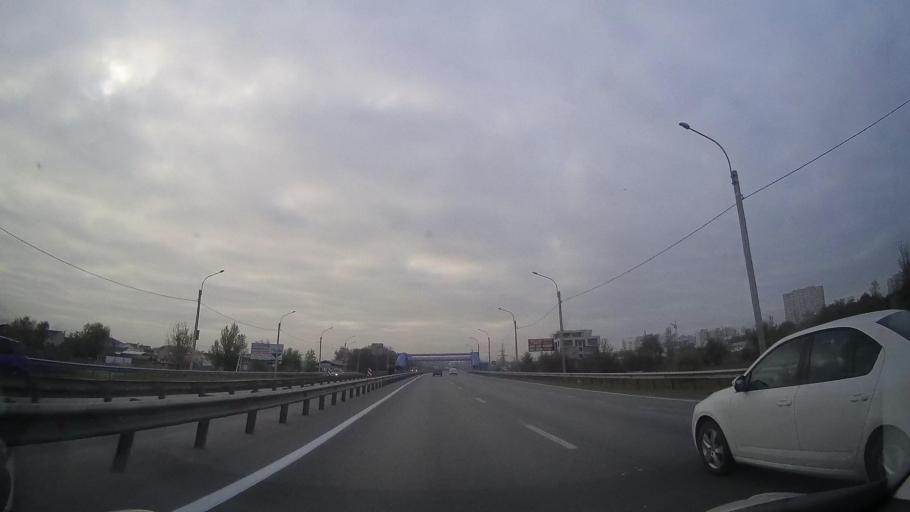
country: RU
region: Rostov
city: Bataysk
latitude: 47.1414
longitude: 39.7760
